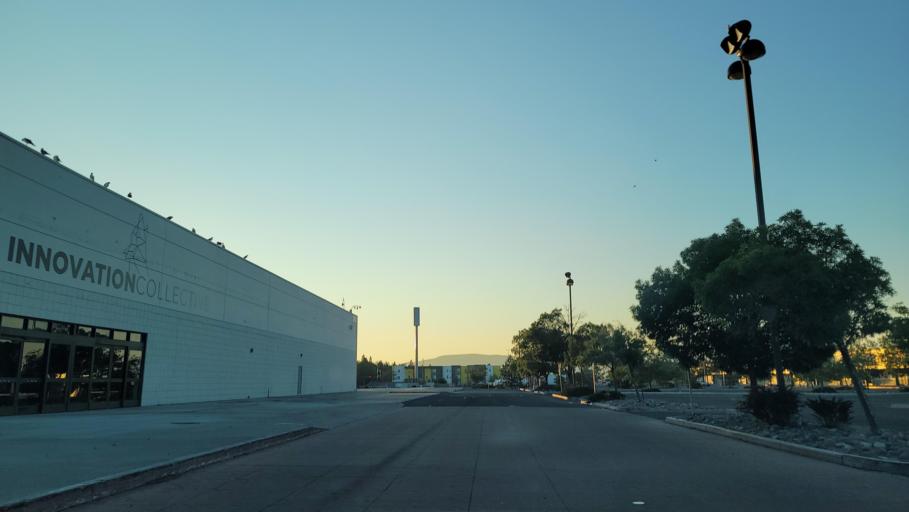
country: US
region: Nevada
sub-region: Washoe County
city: Sparks
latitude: 39.5470
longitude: -119.7797
